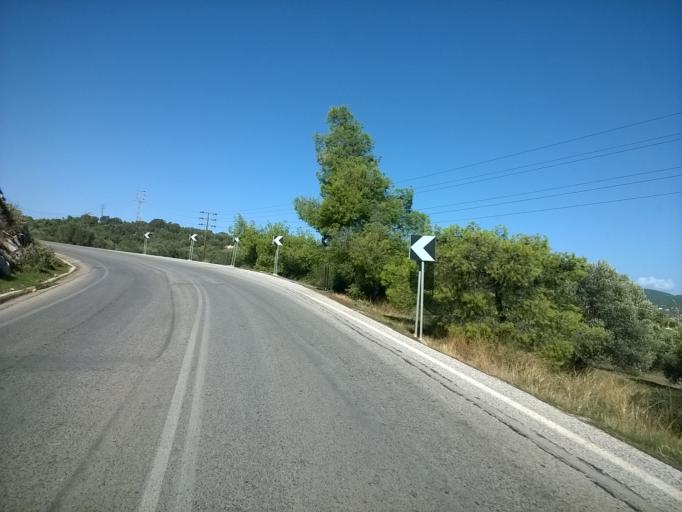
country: GR
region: Attica
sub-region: Nomarchia Anatolikis Attikis
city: Keratea
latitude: 37.7870
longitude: 24.0089
